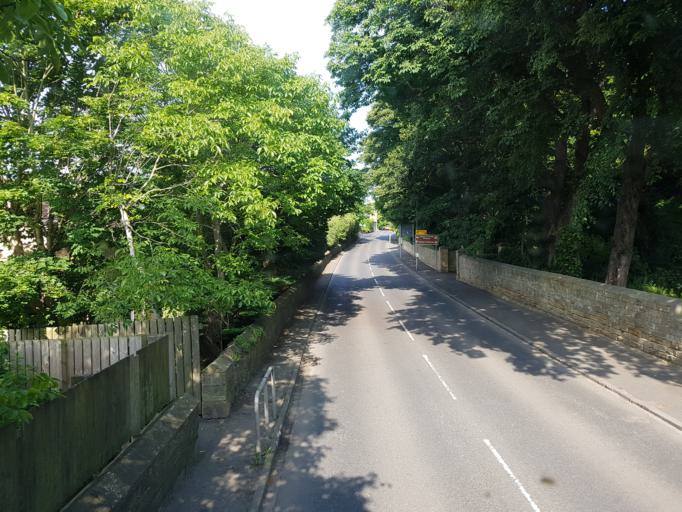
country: GB
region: England
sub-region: Northumberland
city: Alnwick
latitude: 55.4081
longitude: -1.6911
